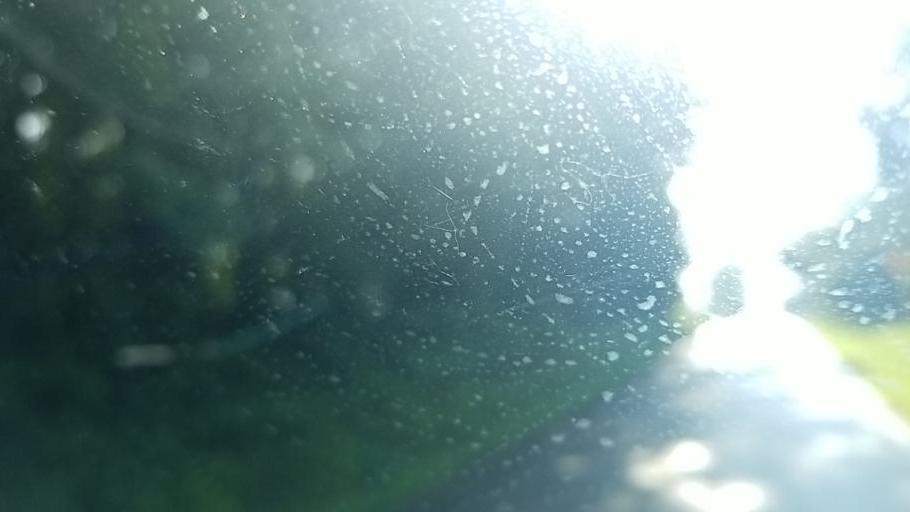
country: US
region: Ohio
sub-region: Wayne County
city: Wooster
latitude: 40.8582
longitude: -81.9798
